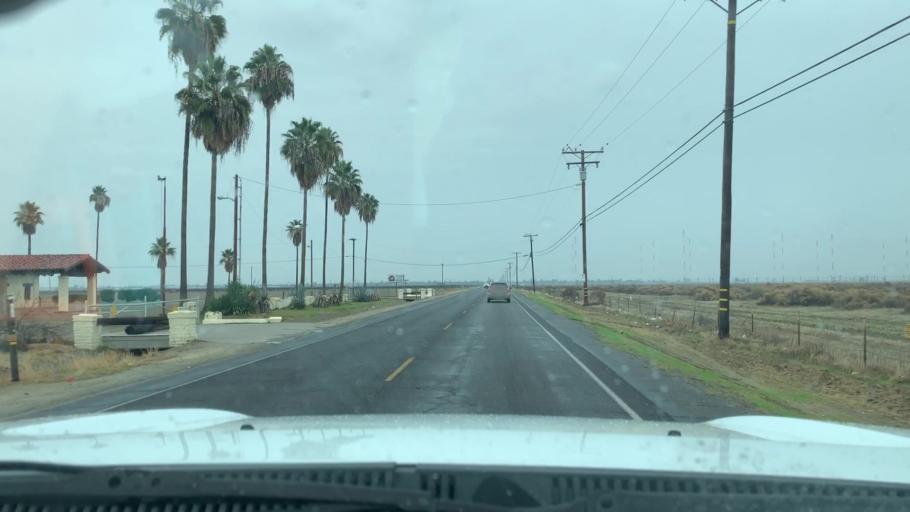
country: US
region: California
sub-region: Kern County
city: Delano
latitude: 35.7613
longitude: -119.2891
